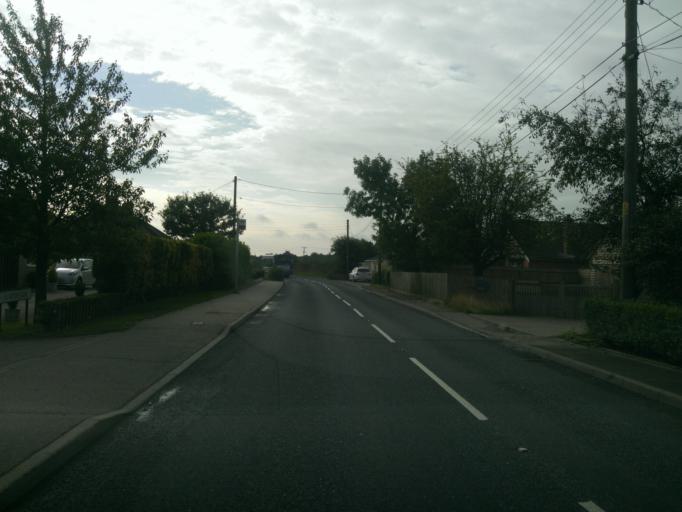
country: GB
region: England
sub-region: Essex
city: Great Bentley
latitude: 51.8389
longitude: 1.0426
